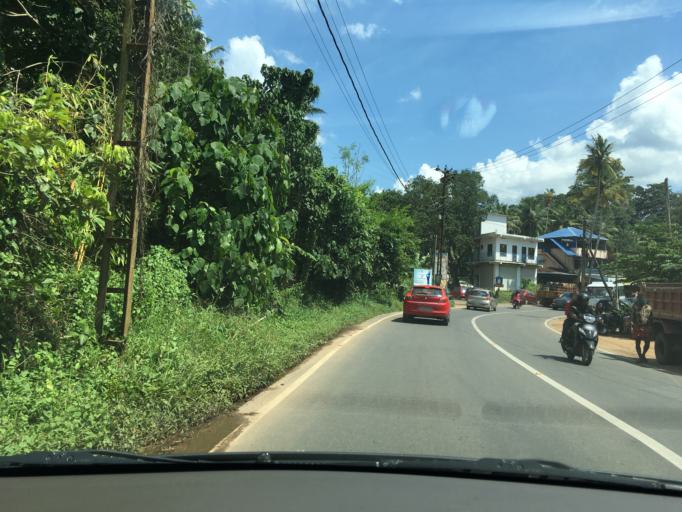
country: IN
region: Kerala
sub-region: Thiruvananthapuram
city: Nedumangad
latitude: 8.6080
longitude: 76.9986
